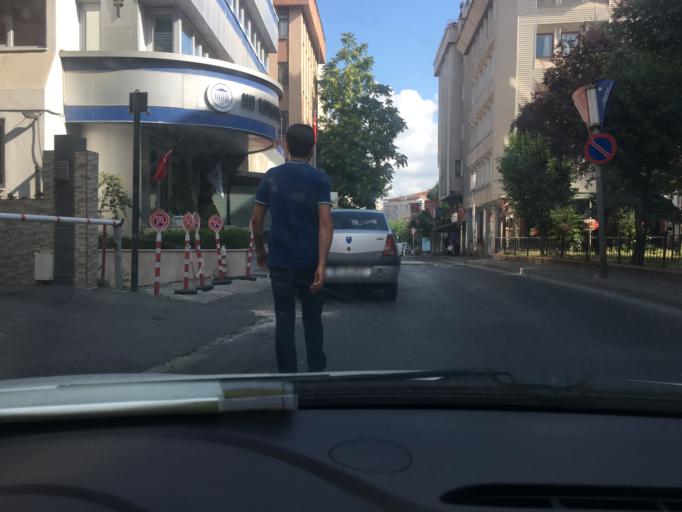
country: TR
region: Istanbul
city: Sisli
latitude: 41.0679
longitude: 29.0032
